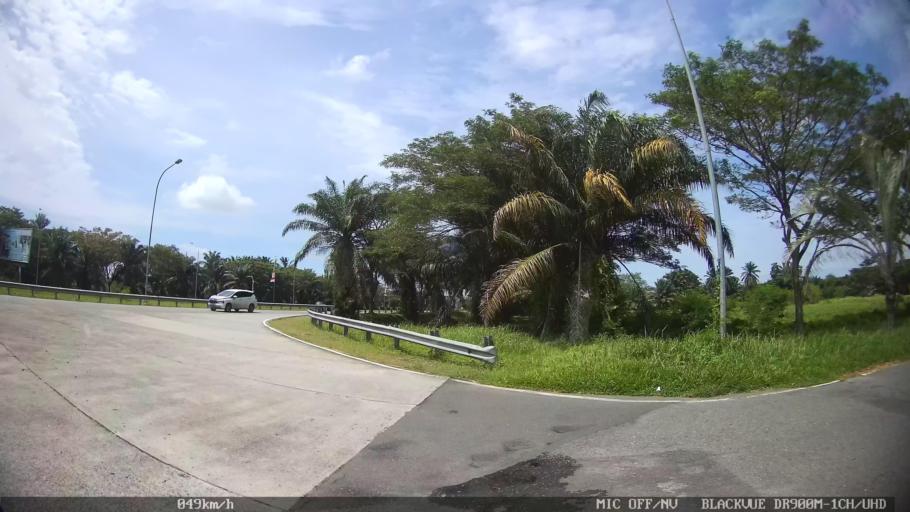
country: ID
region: North Sumatra
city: Percut
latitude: 3.6278
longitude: 98.8699
